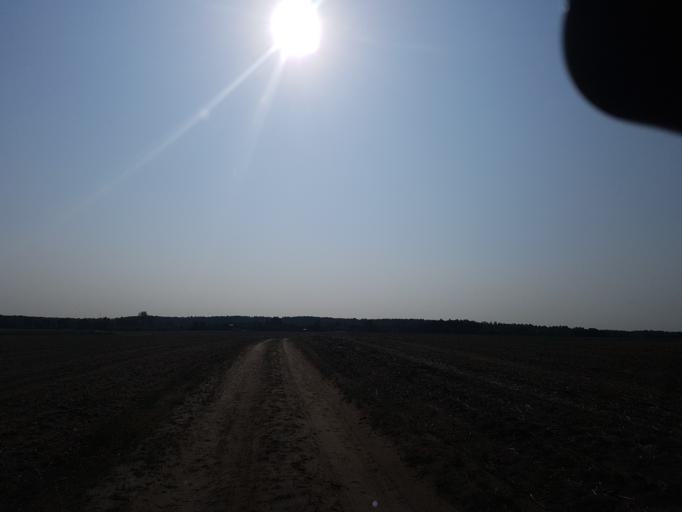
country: DE
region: Brandenburg
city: Wiesenburg
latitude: 52.0610
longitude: 12.3730
